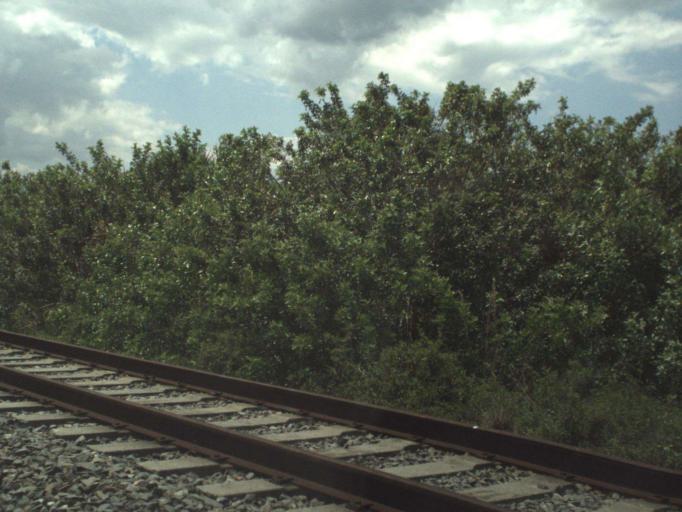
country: US
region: Florida
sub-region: Brevard County
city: Merritt Island
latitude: 28.6435
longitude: -80.6487
